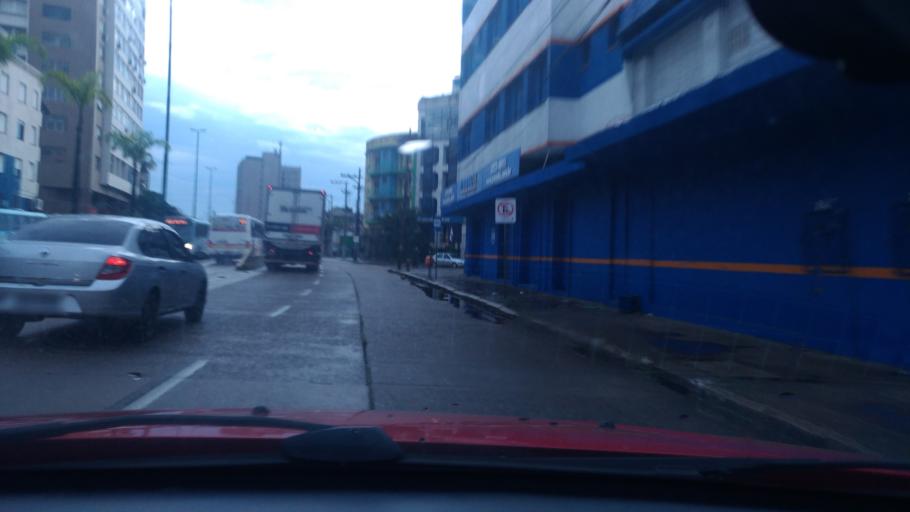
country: BR
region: Rio Grande do Sul
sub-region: Porto Alegre
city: Porto Alegre
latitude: -30.0135
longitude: -51.2039
